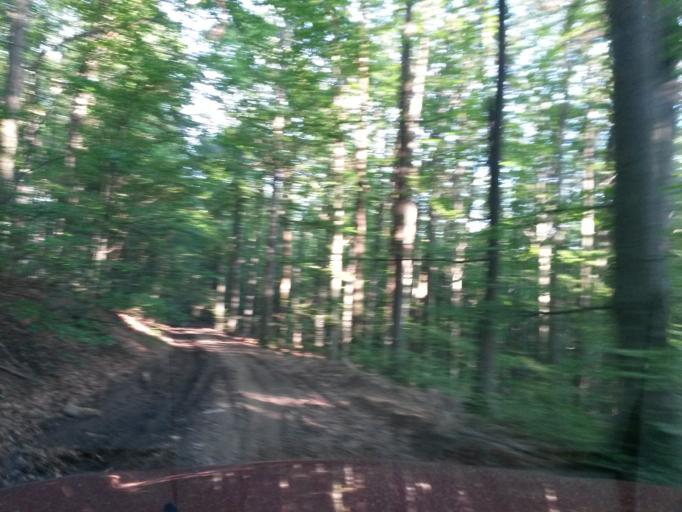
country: SK
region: Kosicky
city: Moldava nad Bodvou
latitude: 48.7315
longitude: 21.0471
